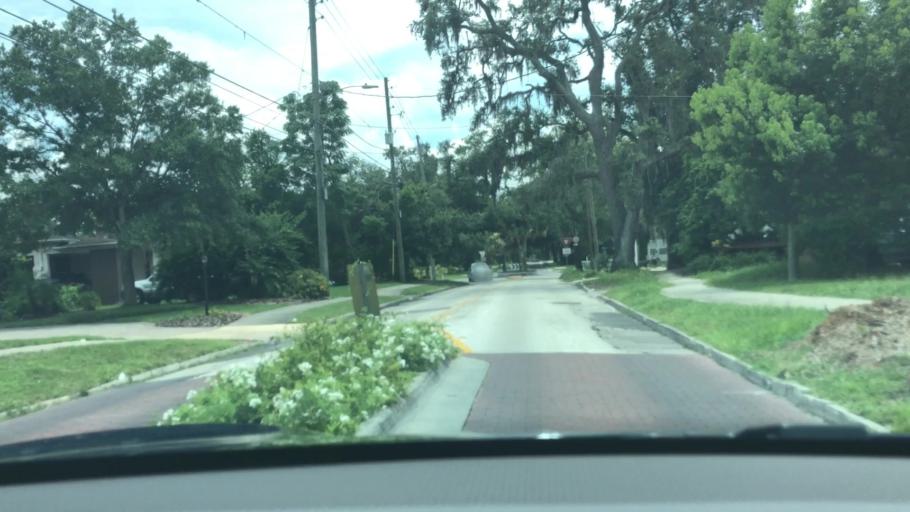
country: US
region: Florida
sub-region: Orange County
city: Orlando
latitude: 28.5174
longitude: -81.3722
